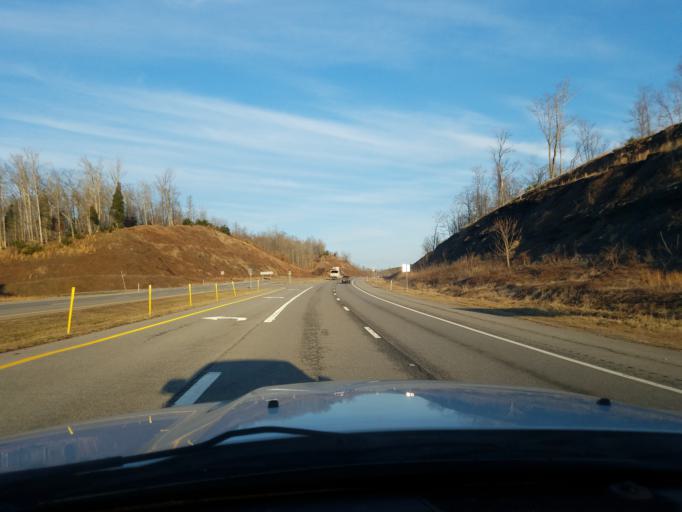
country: US
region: West Virginia
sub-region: Putnam County
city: Buffalo
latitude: 38.5570
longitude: -82.0043
